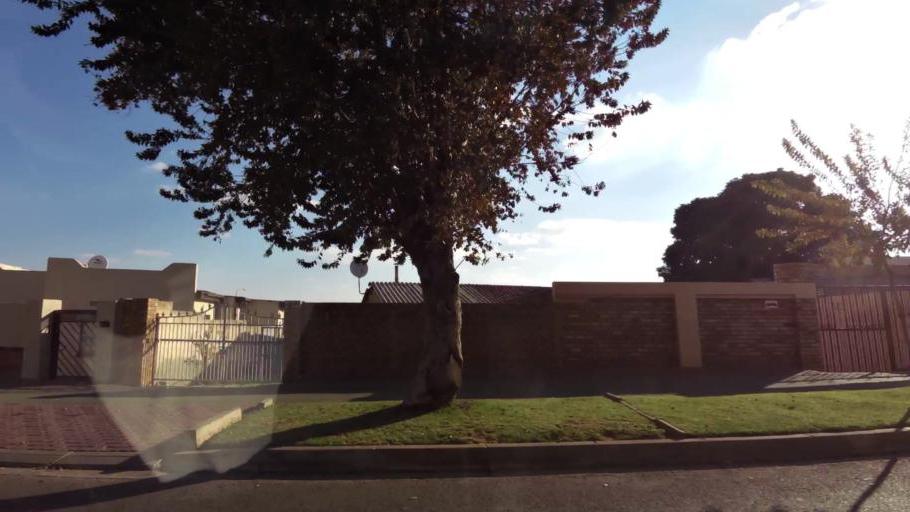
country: ZA
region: Gauteng
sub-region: City of Johannesburg Metropolitan Municipality
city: Roodepoort
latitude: -26.2090
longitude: 27.8844
